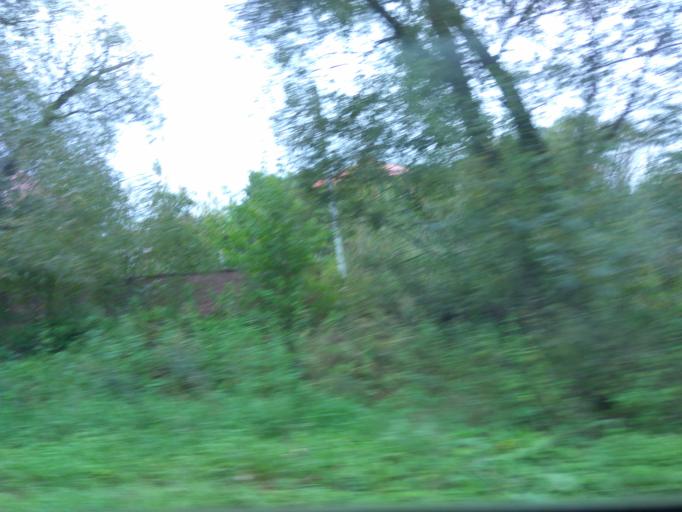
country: RU
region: Moskovskaya
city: Malyshevo
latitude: 55.5346
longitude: 38.3286
